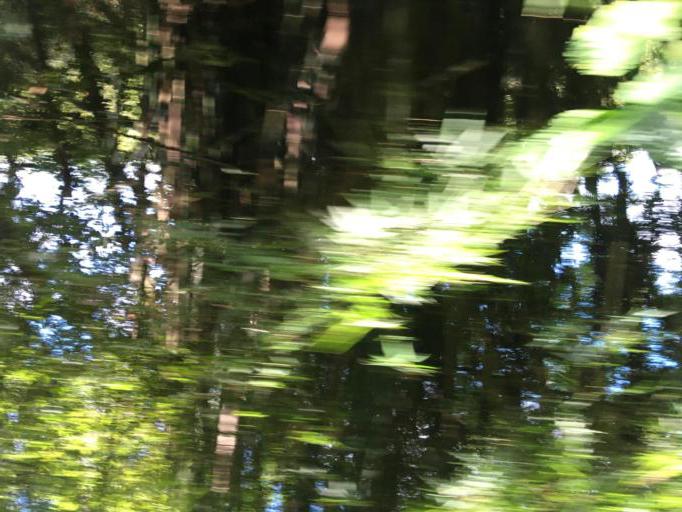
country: TW
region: Taipei
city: Taipei
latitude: 24.9388
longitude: 121.5787
